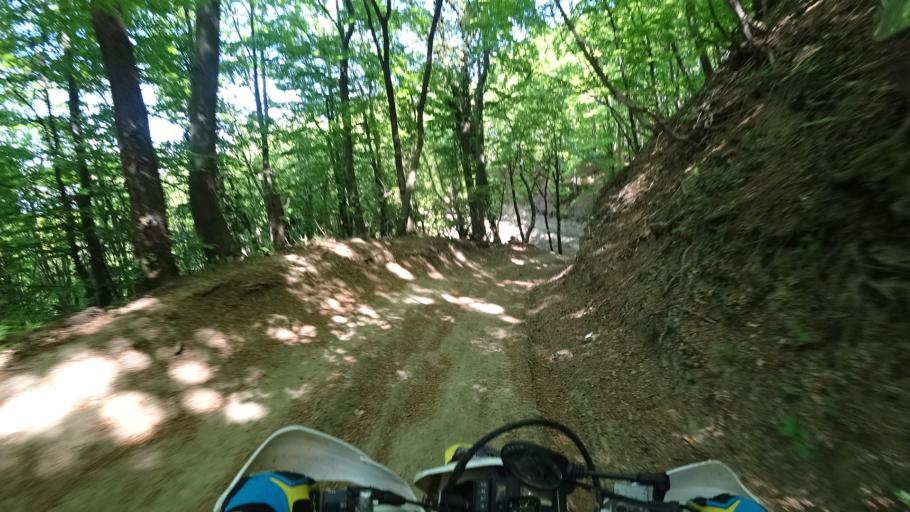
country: HR
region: Zagrebacka
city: Jablanovec
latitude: 45.8626
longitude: 15.8857
